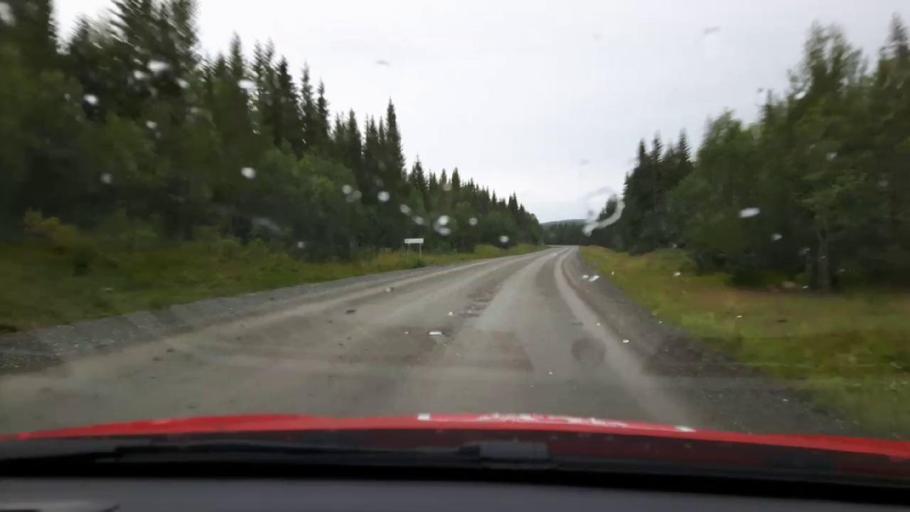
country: SE
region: Jaemtland
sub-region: Are Kommun
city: Are
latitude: 63.4530
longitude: 12.6500
